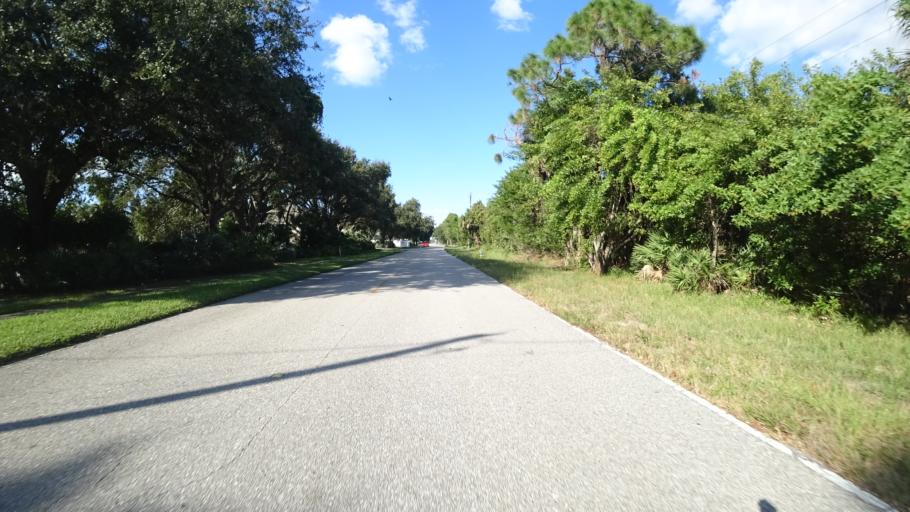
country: US
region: Florida
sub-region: Manatee County
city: Cortez
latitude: 27.4568
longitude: -82.6485
